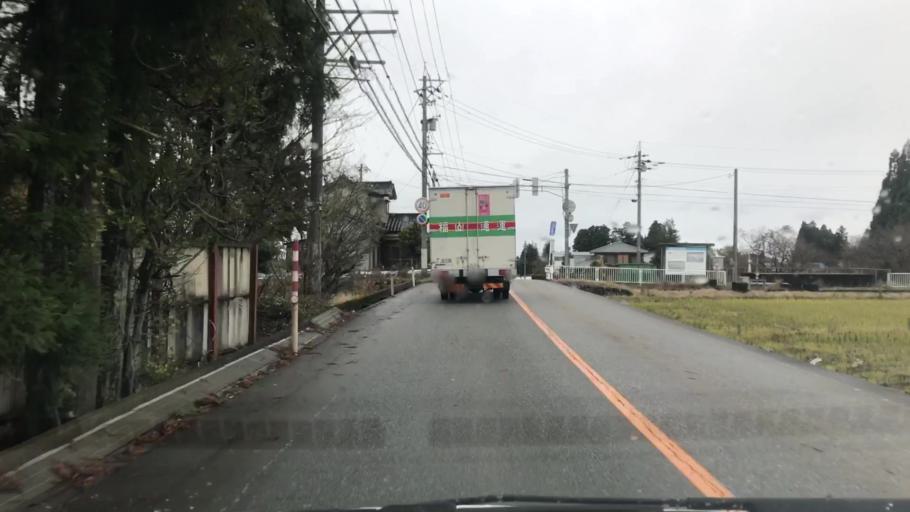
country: JP
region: Toyama
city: Kamiichi
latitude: 36.6011
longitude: 137.3219
